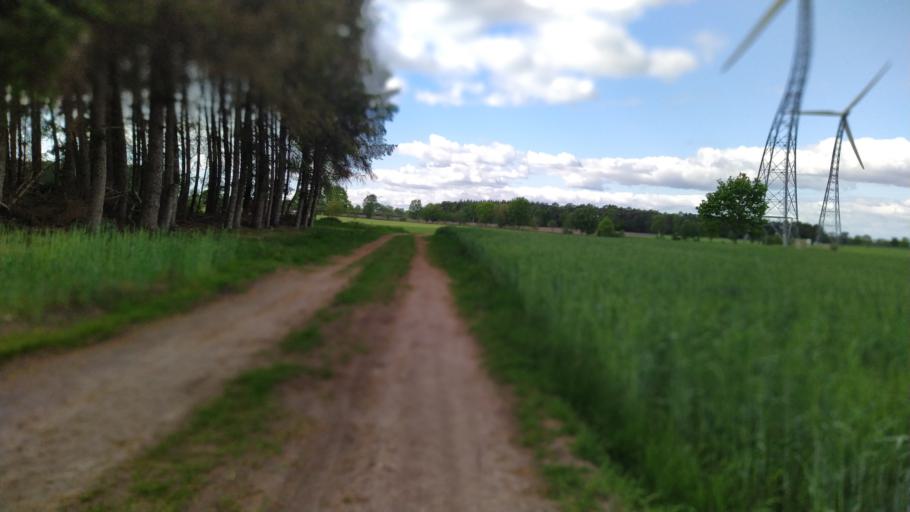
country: DE
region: Lower Saxony
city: Brest
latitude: 53.4371
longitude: 9.3933
